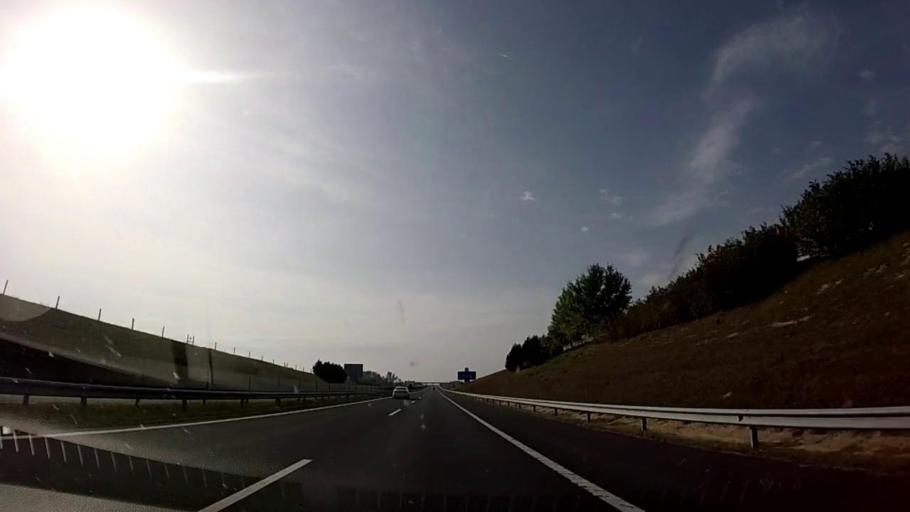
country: HU
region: Zala
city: Nagykanizsa
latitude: 46.4663
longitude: 16.8936
